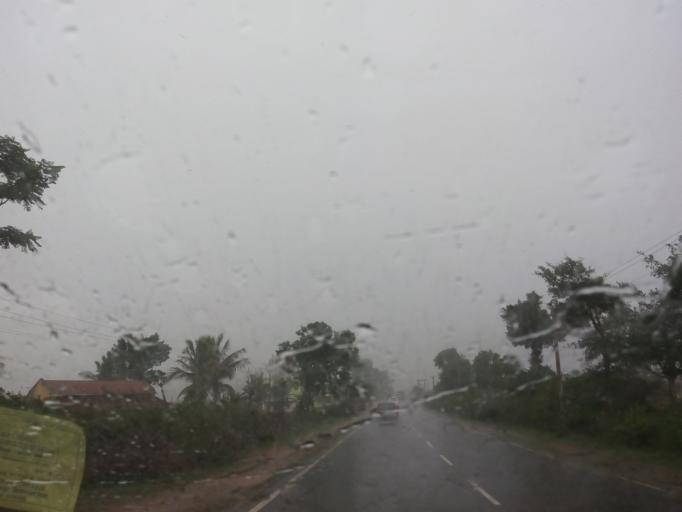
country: IN
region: Karnataka
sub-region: Hassan
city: Belur
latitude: 13.1217
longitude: 75.9976
